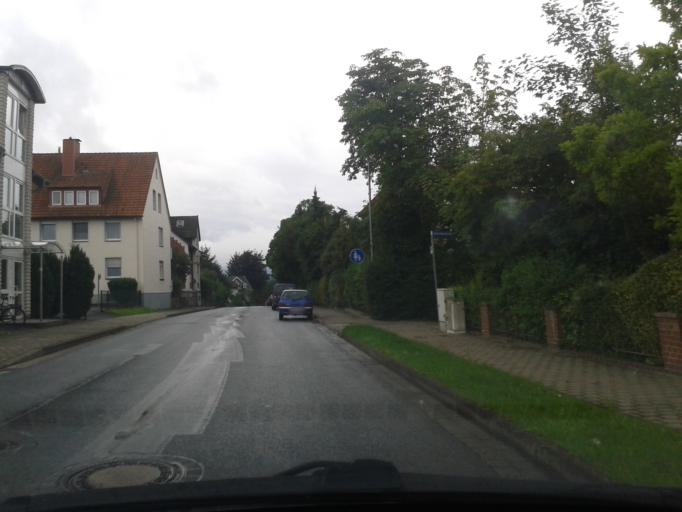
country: DE
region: North Rhine-Westphalia
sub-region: Regierungsbezirk Detmold
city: Detmold
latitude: 51.9430
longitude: 8.8923
